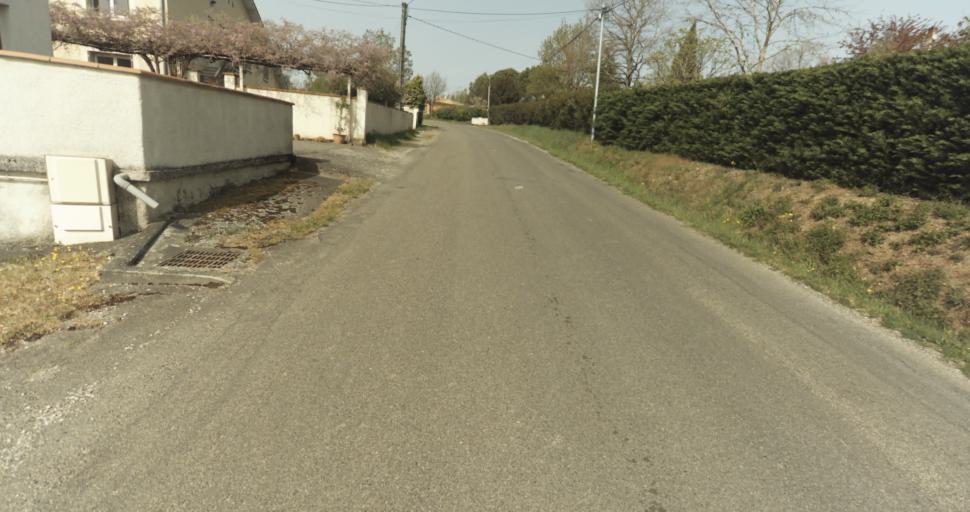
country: FR
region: Midi-Pyrenees
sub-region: Departement du Tarn-et-Garonne
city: Moissac
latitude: 44.1199
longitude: 1.0963
